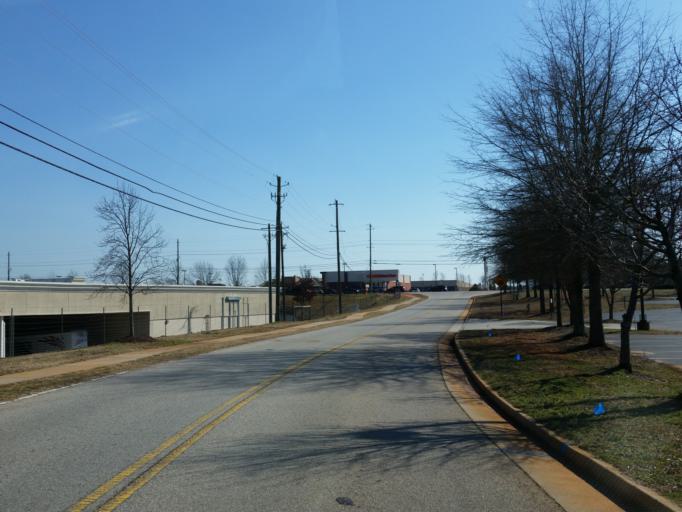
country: US
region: Georgia
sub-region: Henry County
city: McDonough
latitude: 33.4660
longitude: -84.2217
